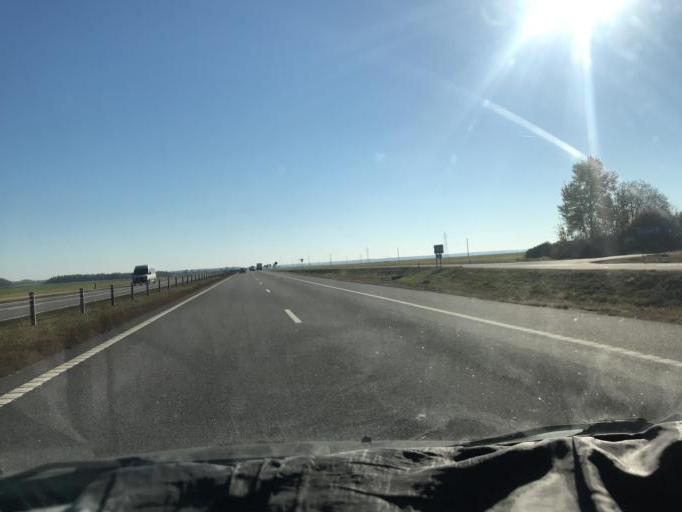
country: BY
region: Mogilev
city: Yalizava
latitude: 53.2430
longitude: 28.9481
